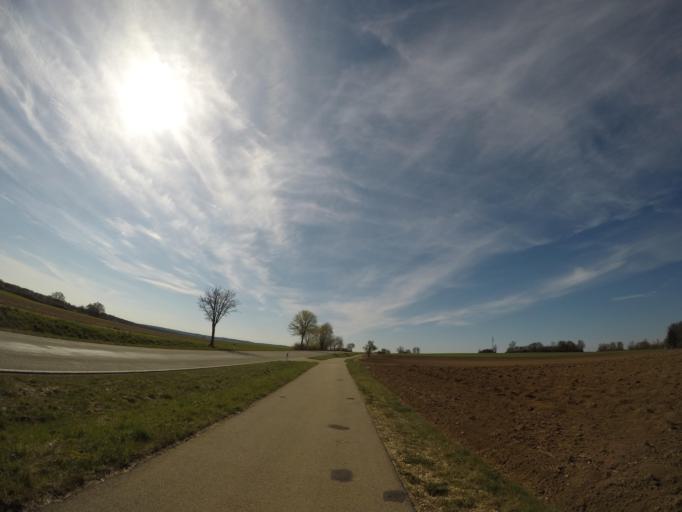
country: DE
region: Baden-Wuerttemberg
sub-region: Tuebingen Region
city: Mehrstetten
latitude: 48.3434
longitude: 9.6061
